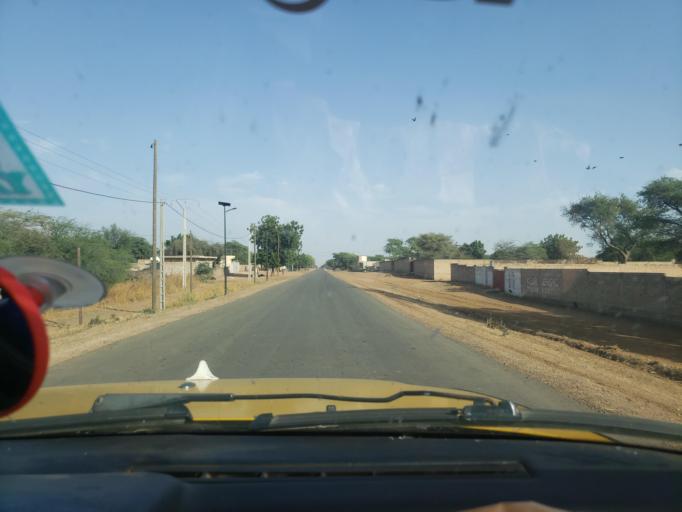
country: SN
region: Louga
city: Louga
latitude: 15.5118
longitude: -15.9897
